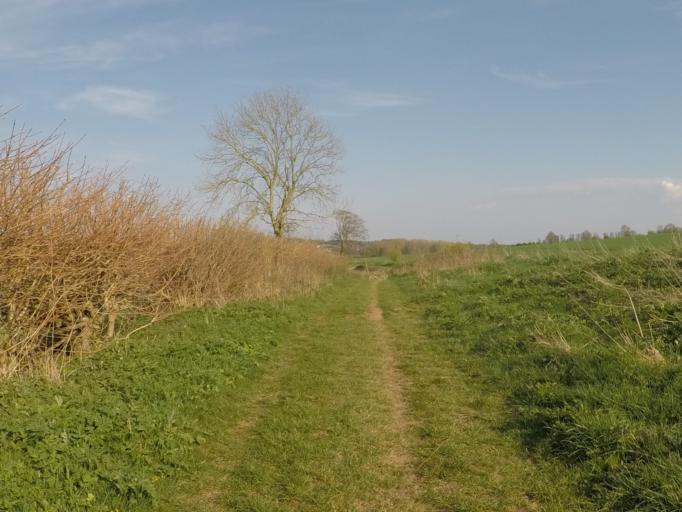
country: GB
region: England
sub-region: Oxfordshire
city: Charlbury
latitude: 51.8756
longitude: -1.5064
